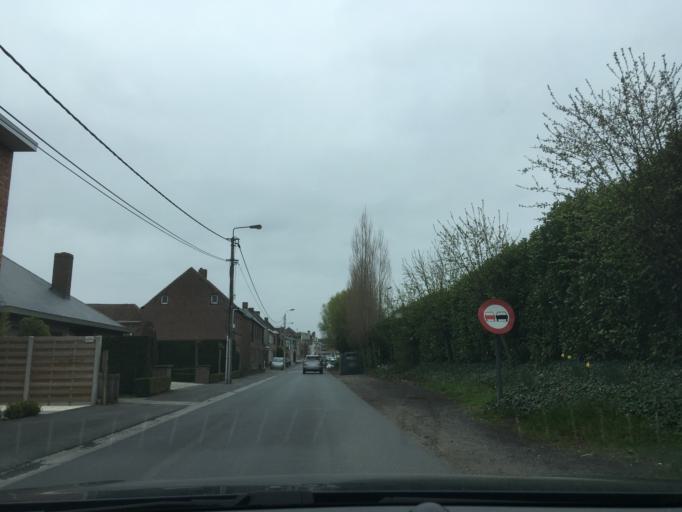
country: BE
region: Flanders
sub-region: Provincie West-Vlaanderen
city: Lichtervelde
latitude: 51.0271
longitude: 3.1245
